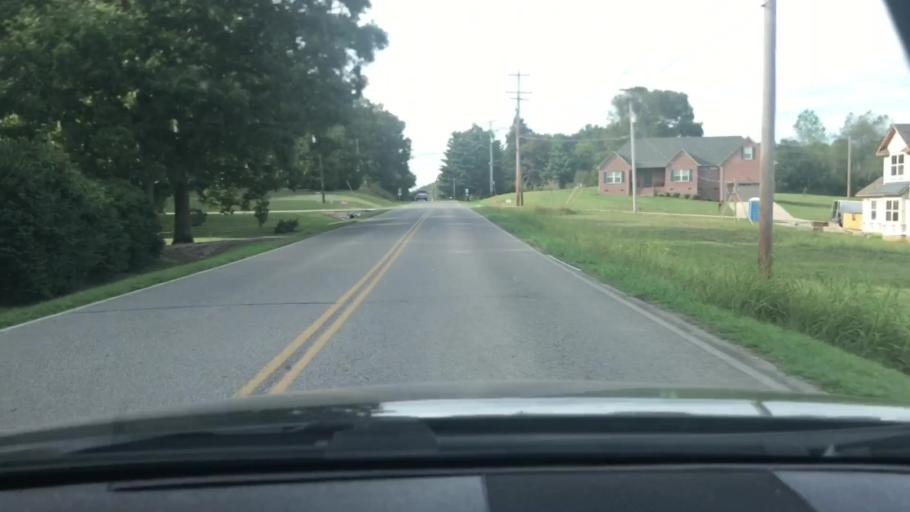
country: US
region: Tennessee
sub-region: Dickson County
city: White Bluff
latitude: 36.0937
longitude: -87.2138
